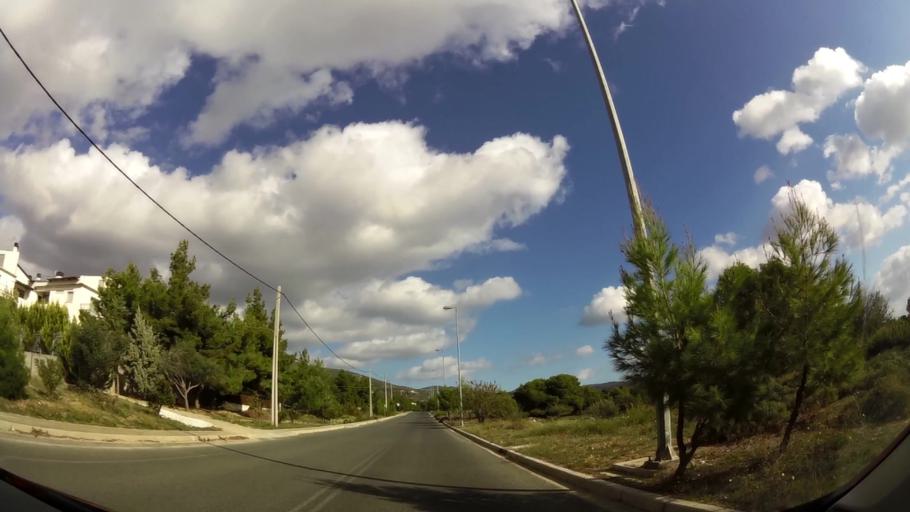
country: GR
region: Attica
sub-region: Nomarchia Anatolikis Attikis
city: Thrakomakedones
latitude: 38.1267
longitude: 23.7675
